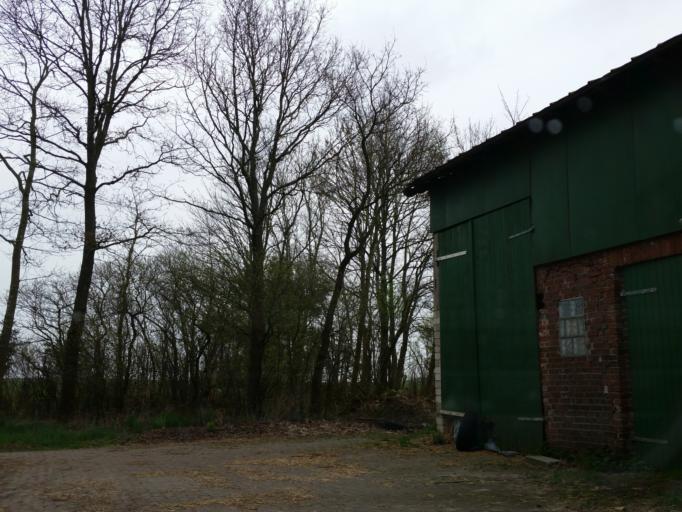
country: DE
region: Lower Saxony
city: Alfstedt
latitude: 53.5647
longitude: 9.0232
